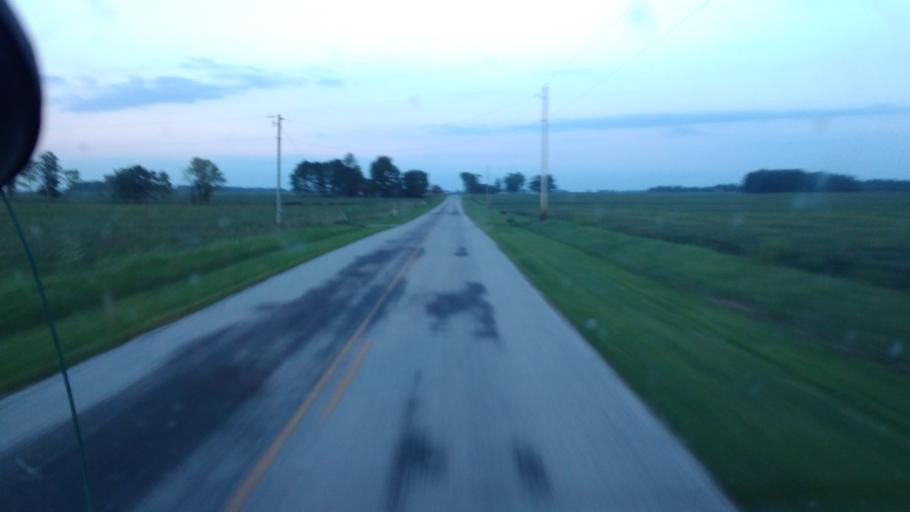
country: US
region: Ohio
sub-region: Hardin County
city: Kenton
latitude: 40.6722
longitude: -83.4861
